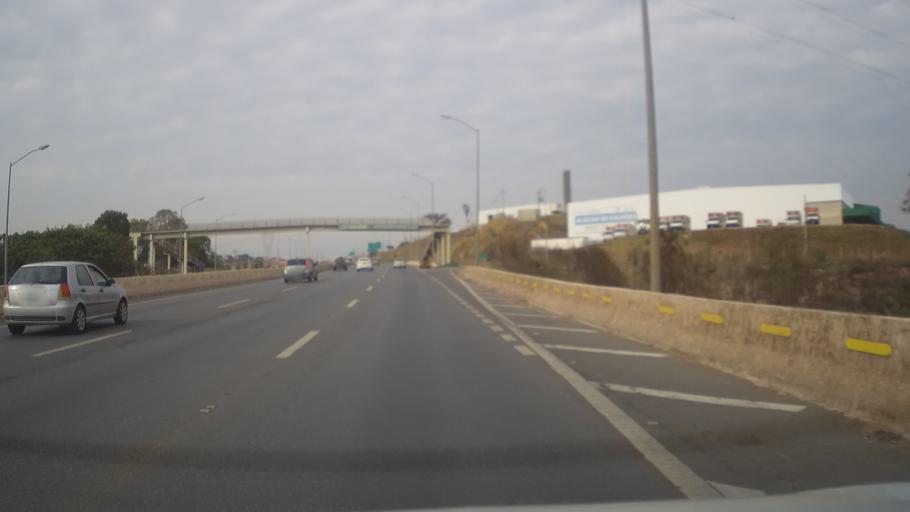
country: BR
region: Minas Gerais
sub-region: Vespasiano
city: Vespasiano
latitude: -19.7328
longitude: -43.9438
